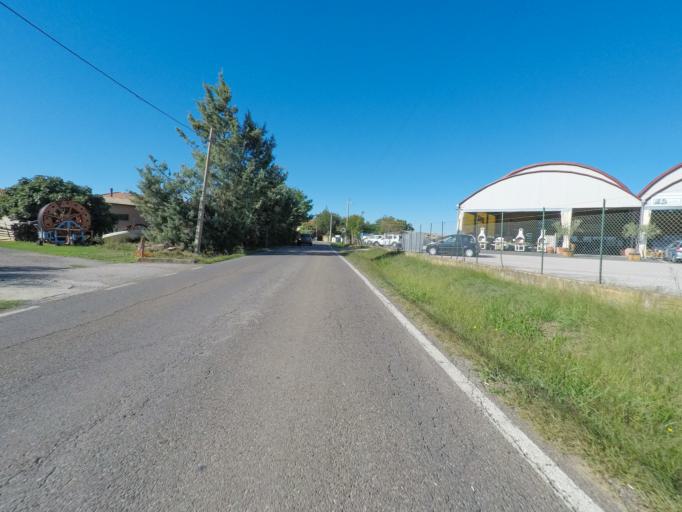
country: IT
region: Tuscany
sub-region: Provincia di Grosseto
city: Grosseto
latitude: 42.7689
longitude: 11.1422
